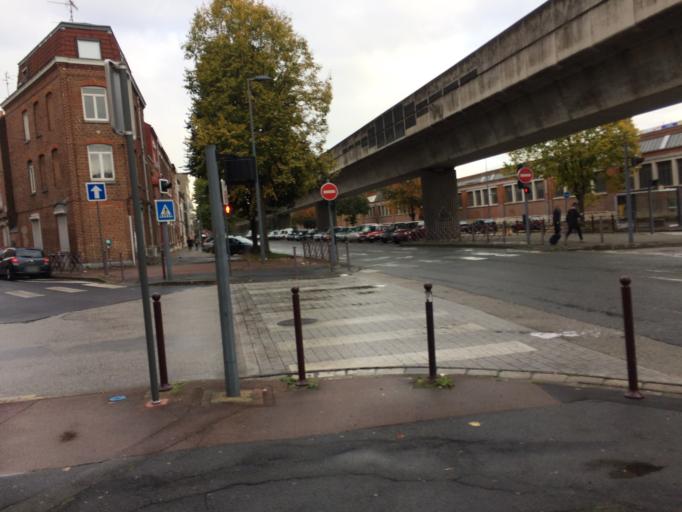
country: FR
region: Nord-Pas-de-Calais
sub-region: Departement du Nord
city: Lille
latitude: 50.6178
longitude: 3.0667
